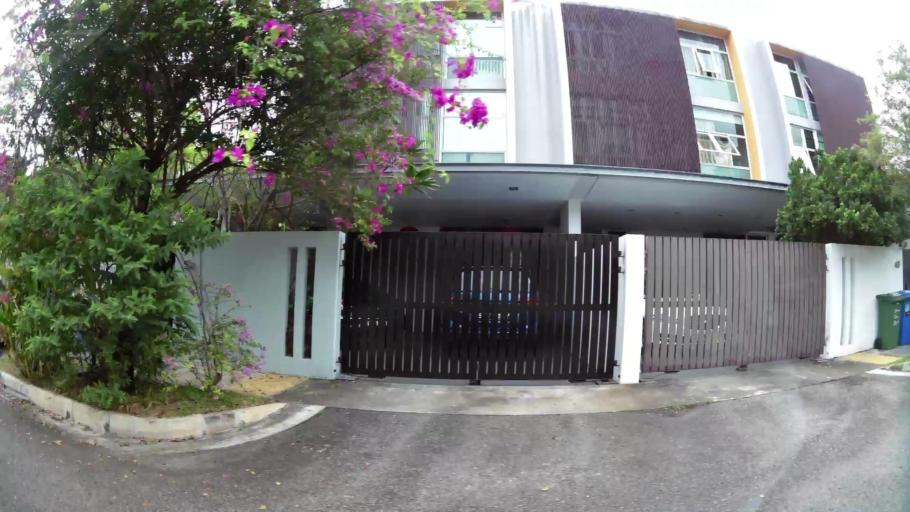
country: SG
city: Singapore
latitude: 1.3610
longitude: 103.8757
